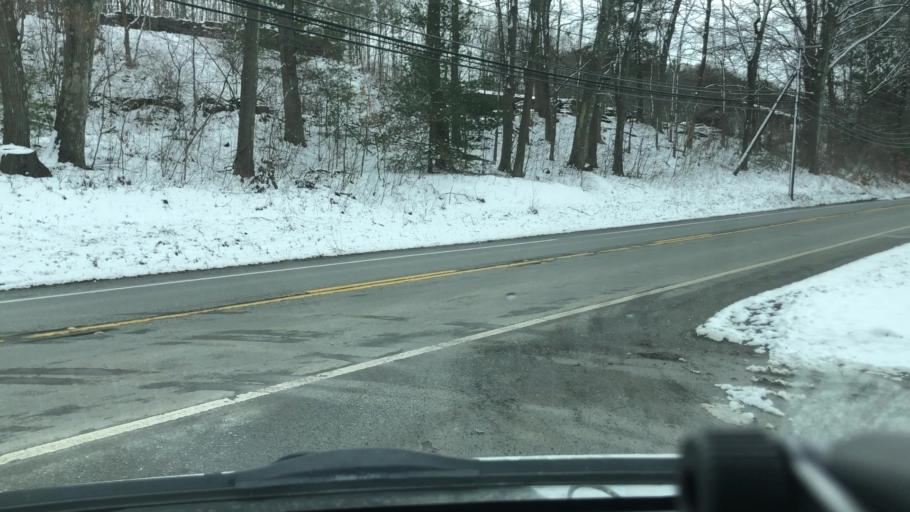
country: US
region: Massachusetts
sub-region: Franklin County
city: Greenfield
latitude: 42.5661
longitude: -72.5928
